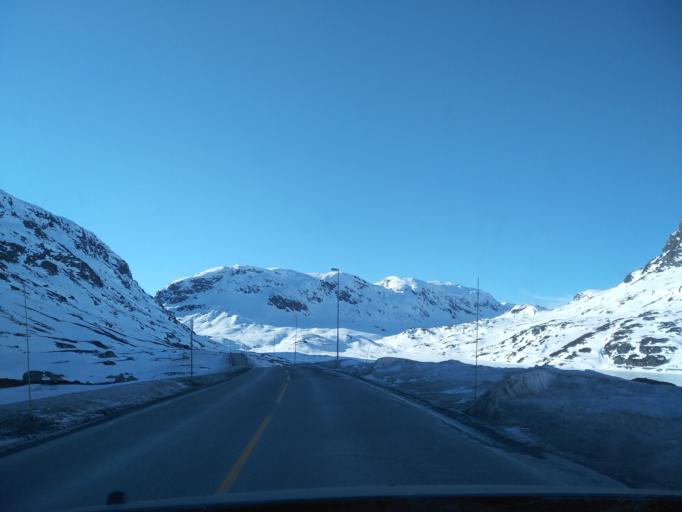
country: NO
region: Aust-Agder
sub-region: Bykle
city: Hovden
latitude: 59.8510
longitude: 7.1000
